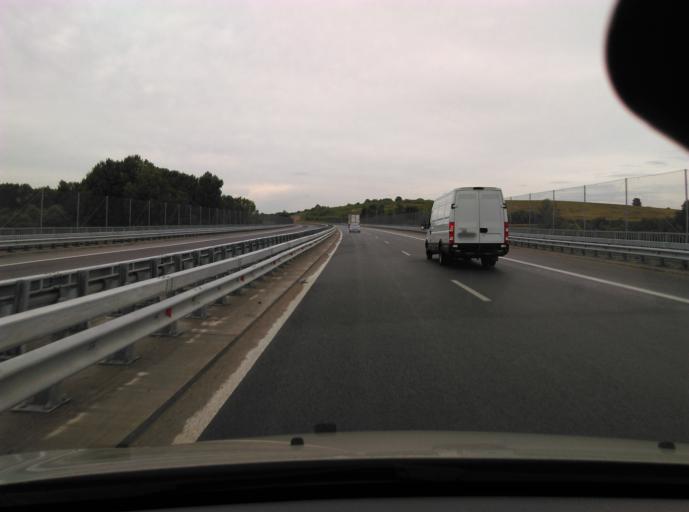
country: BG
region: Stara Zagora
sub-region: Obshtina Chirpan
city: Chirpan
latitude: 42.0917
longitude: 25.4473
